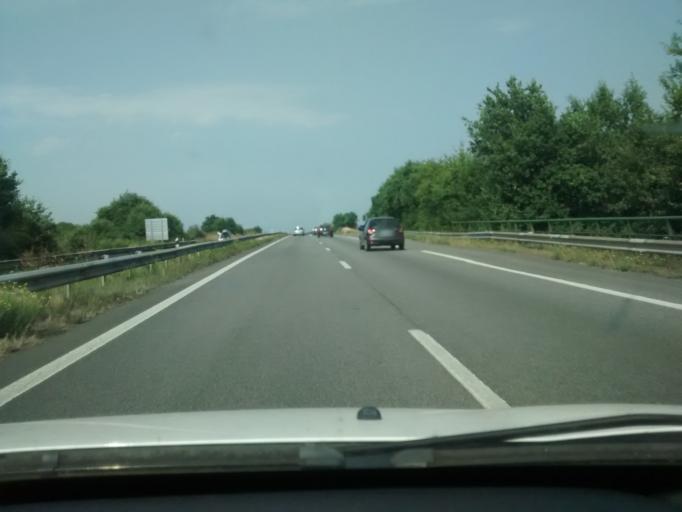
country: FR
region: Pays de la Loire
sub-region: Departement de la Loire-Atlantique
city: Prinquiau
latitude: 47.3575
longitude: -2.0194
